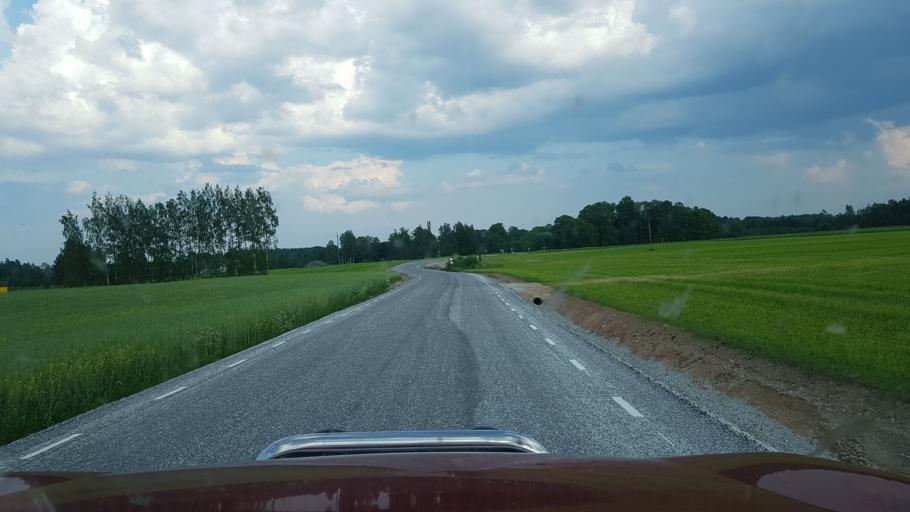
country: EE
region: Tartu
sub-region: UElenurme vald
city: Ulenurme
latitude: 58.0912
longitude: 26.8107
